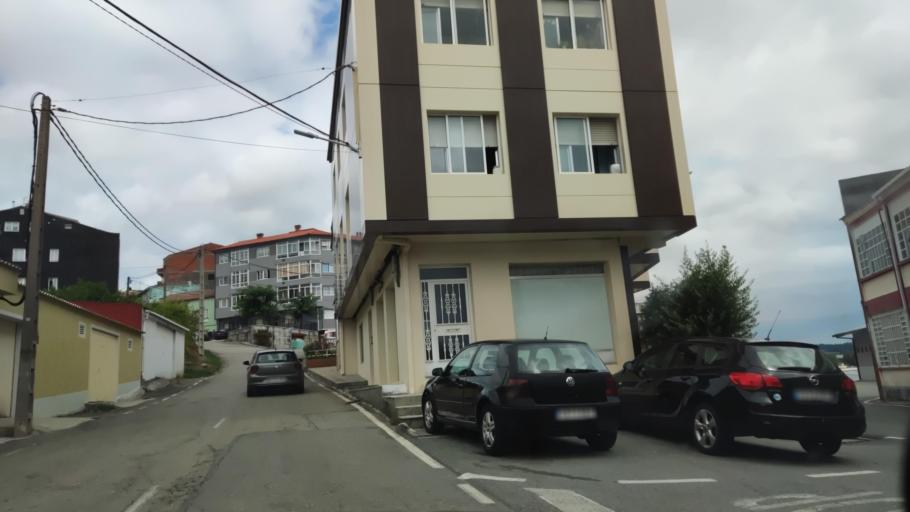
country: ES
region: Galicia
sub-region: Provincia da Coruna
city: Boiro
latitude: 42.6369
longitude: -8.9029
